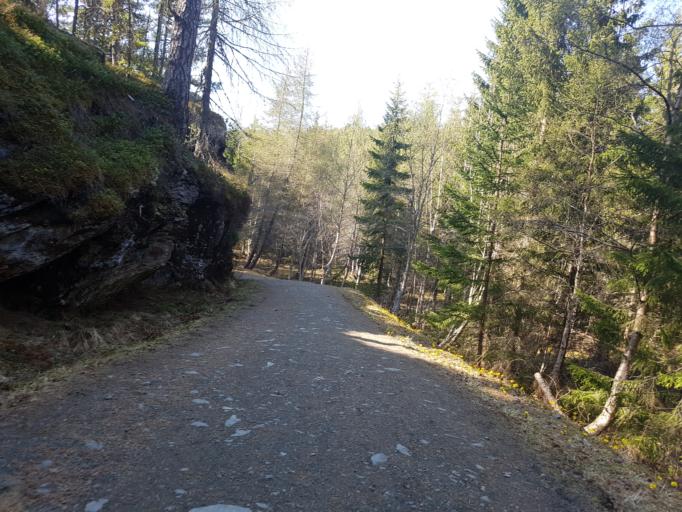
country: NO
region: Sor-Trondelag
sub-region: Trondheim
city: Trondheim
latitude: 63.4401
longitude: 10.3353
